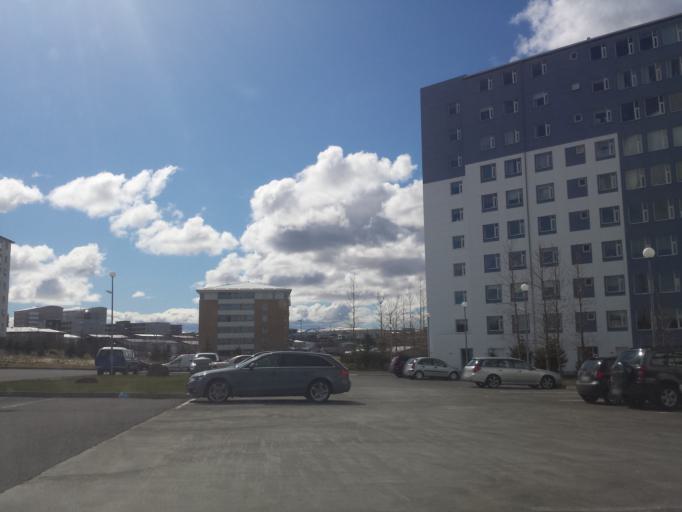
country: IS
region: Capital Region
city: Reykjavik
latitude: 64.0954
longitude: -21.8534
